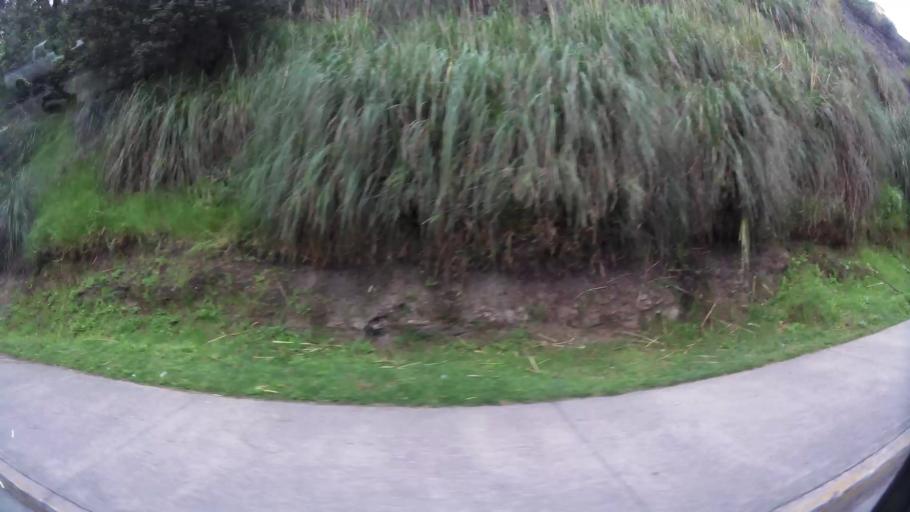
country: EC
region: Pichincha
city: Quito
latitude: -0.2306
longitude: -78.5083
